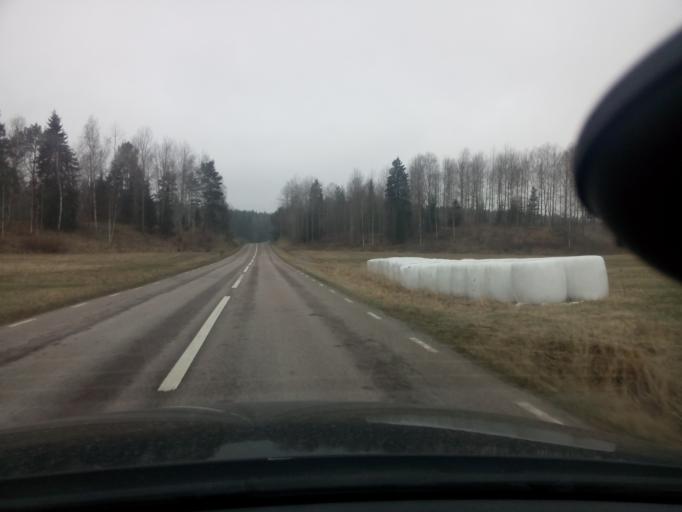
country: SE
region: Soedermanland
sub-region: Gnesta Kommun
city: Gnesta
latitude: 58.9961
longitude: 17.1708
